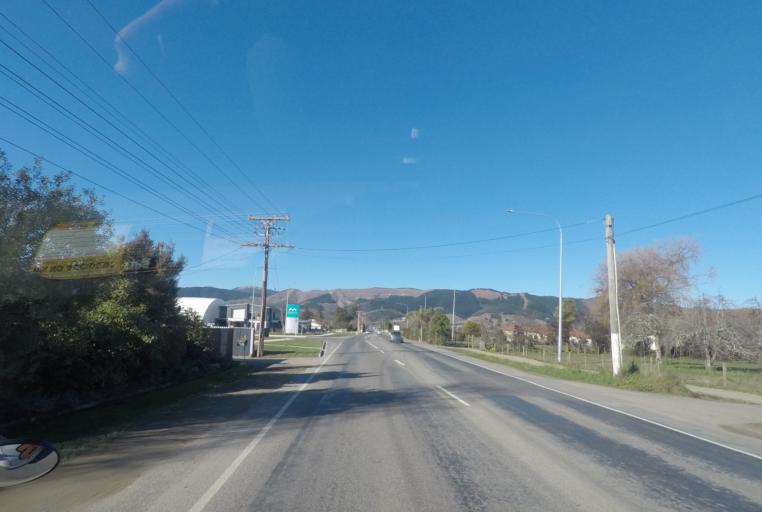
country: NZ
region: Tasman
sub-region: Tasman District
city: Richmond
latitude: -41.3292
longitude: 173.1736
